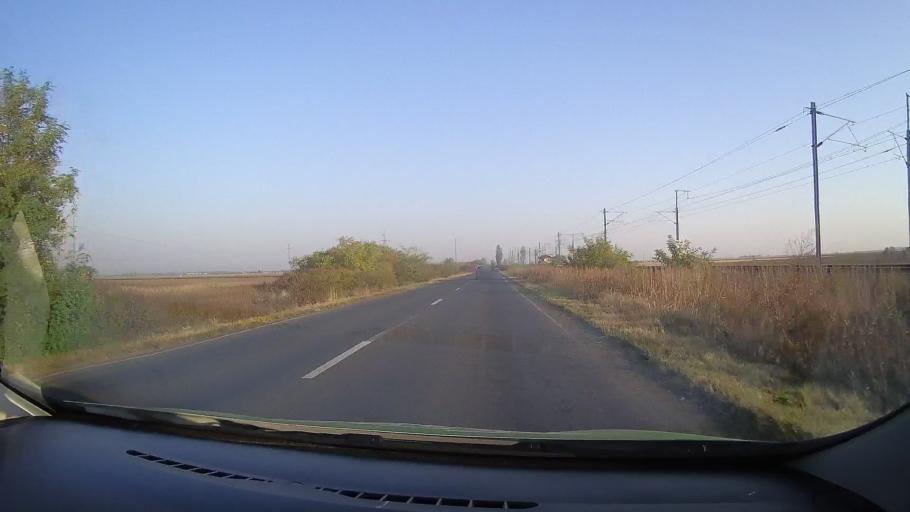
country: RO
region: Arad
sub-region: Comuna Sofronea
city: Sofronea
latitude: 46.2587
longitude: 21.3177
